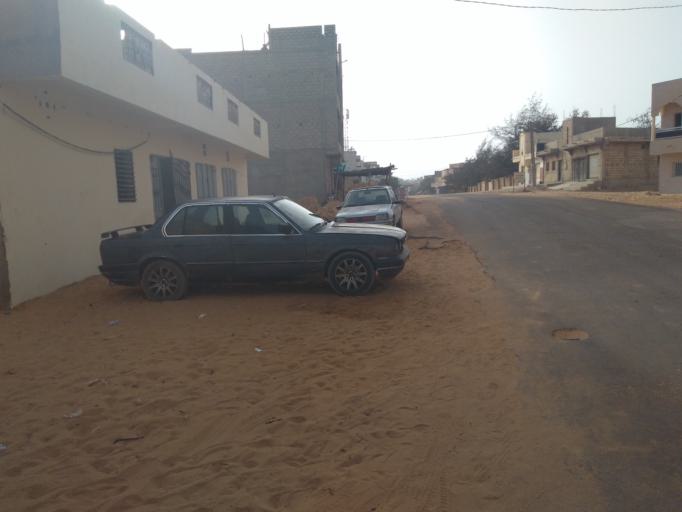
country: SN
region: Dakar
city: Pikine
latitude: 14.8024
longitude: -17.3409
